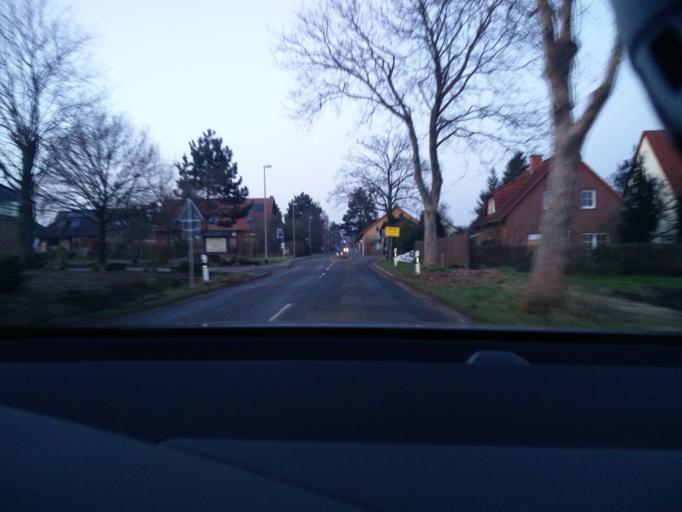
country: DE
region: Lower Saxony
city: Laatzen
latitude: 52.3256
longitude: 9.8499
